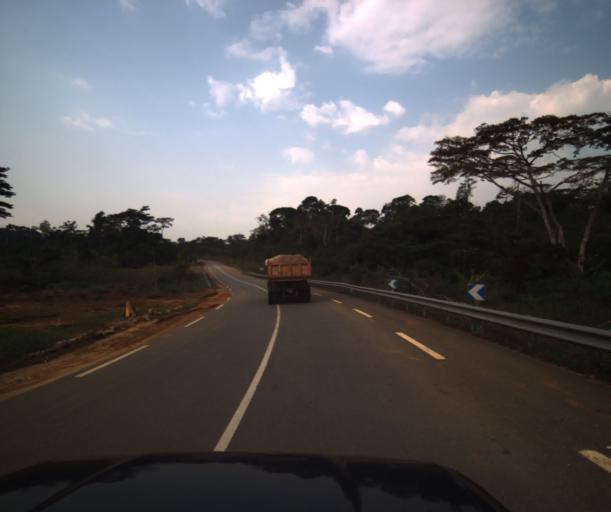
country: CM
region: Centre
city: Mbankomo
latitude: 3.6555
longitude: 11.3407
